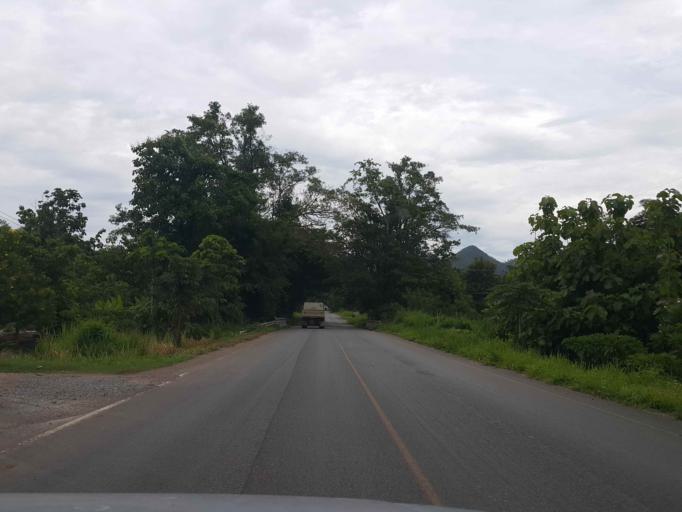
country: TH
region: Lampang
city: Thoen
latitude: 17.5456
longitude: 99.3381
